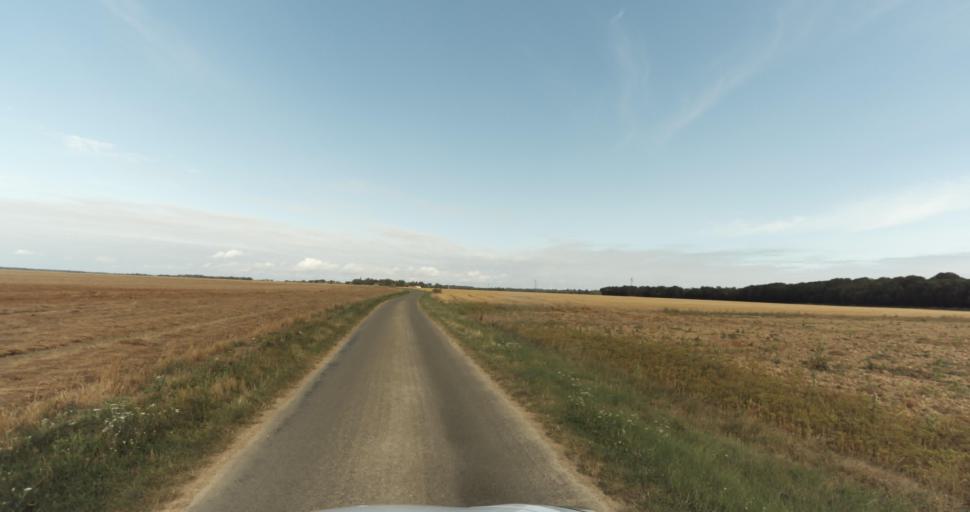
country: FR
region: Haute-Normandie
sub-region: Departement de l'Eure
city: Nonancourt
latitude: 48.8221
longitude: 1.1598
